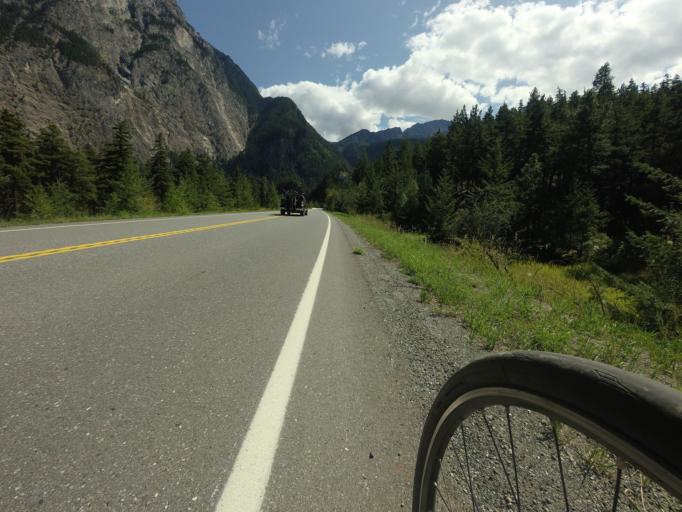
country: CA
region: British Columbia
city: Lillooet
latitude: 50.6637
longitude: -121.9882
